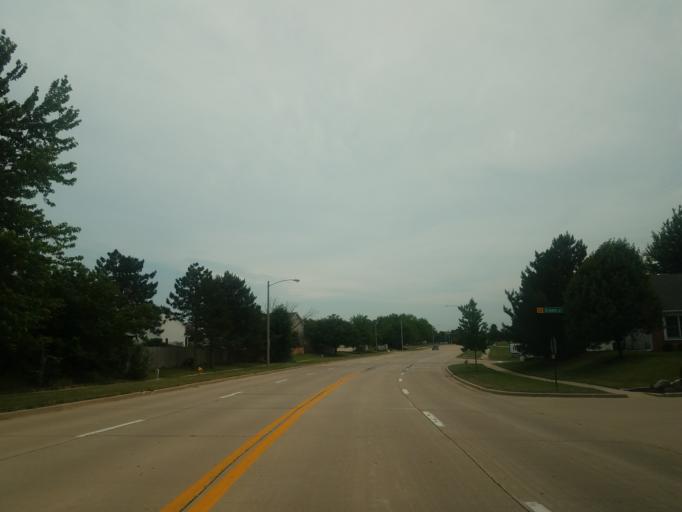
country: US
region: Illinois
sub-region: McLean County
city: Normal
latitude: 40.5136
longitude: -88.9421
